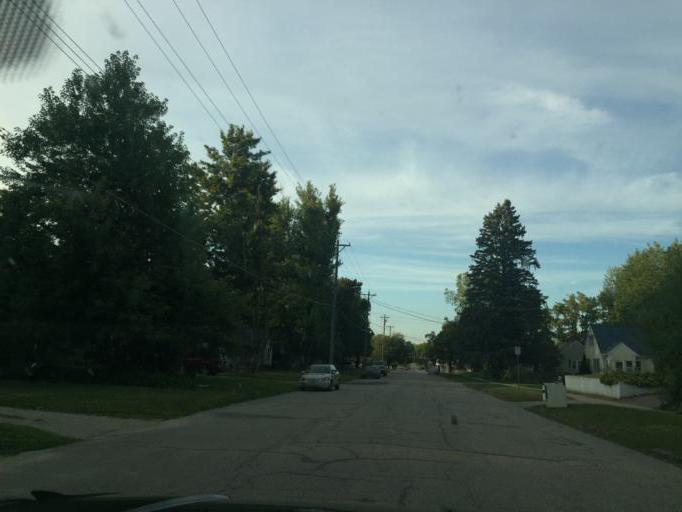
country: US
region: Minnesota
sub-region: Olmsted County
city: Rochester
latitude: 44.0192
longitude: -92.4921
